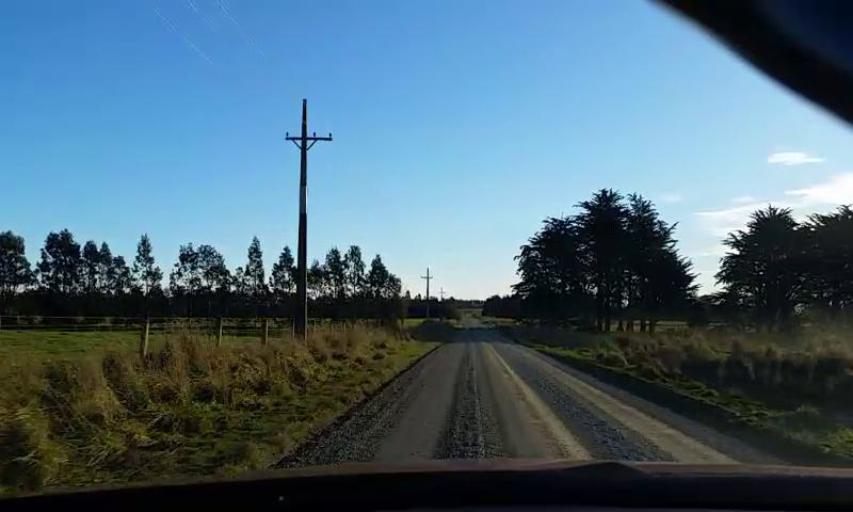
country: NZ
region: Southland
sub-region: Invercargill City
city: Invercargill
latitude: -46.2916
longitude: 168.4197
